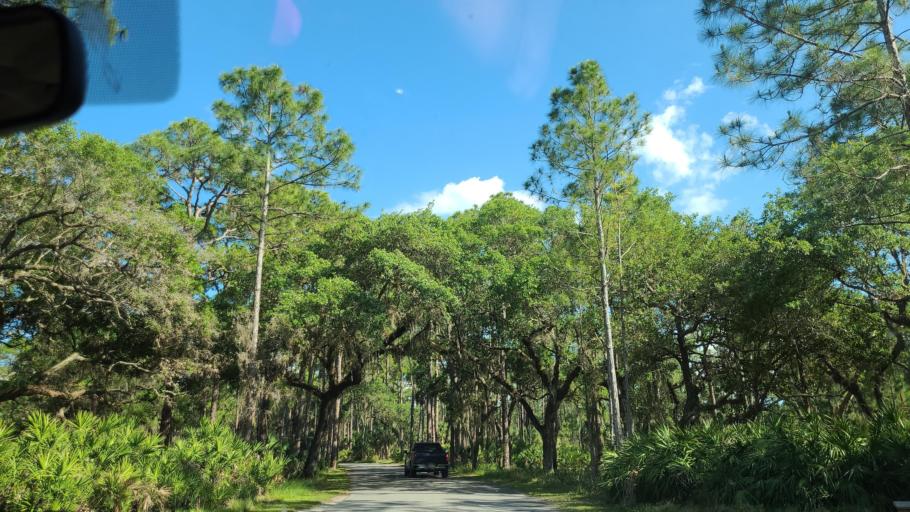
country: US
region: Florida
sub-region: Polk County
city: Babson Park
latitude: 27.9482
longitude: -81.3567
